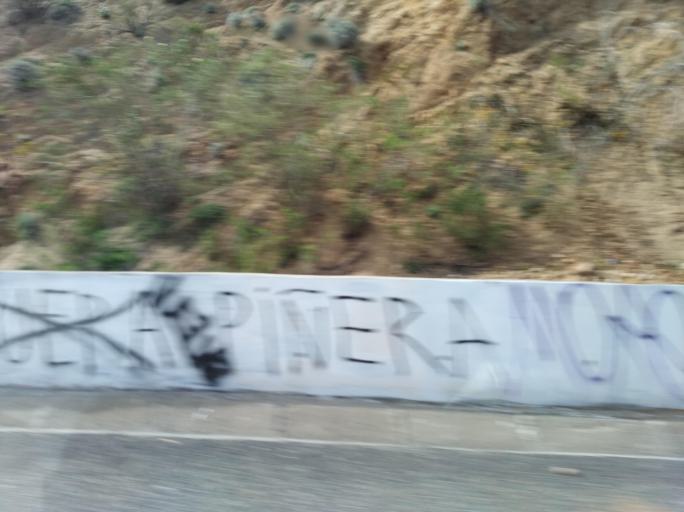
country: CL
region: Valparaiso
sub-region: Provincia de San Felipe
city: Llaillay
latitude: -33.0656
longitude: -71.0180
